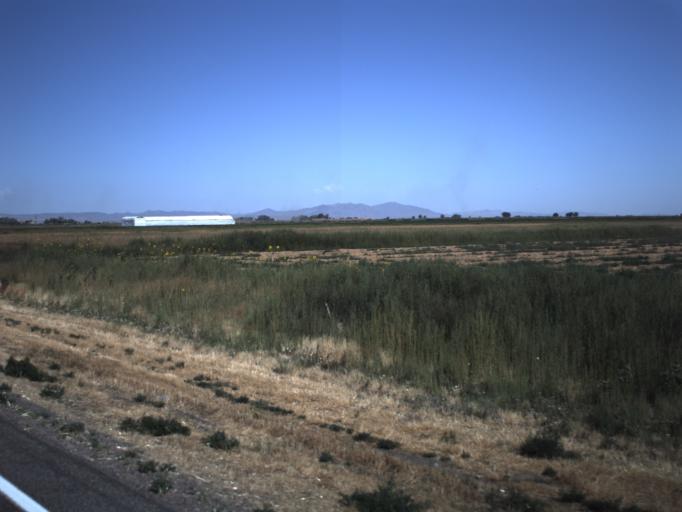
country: US
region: Utah
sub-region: Millard County
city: Delta
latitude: 39.3307
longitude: -112.6445
